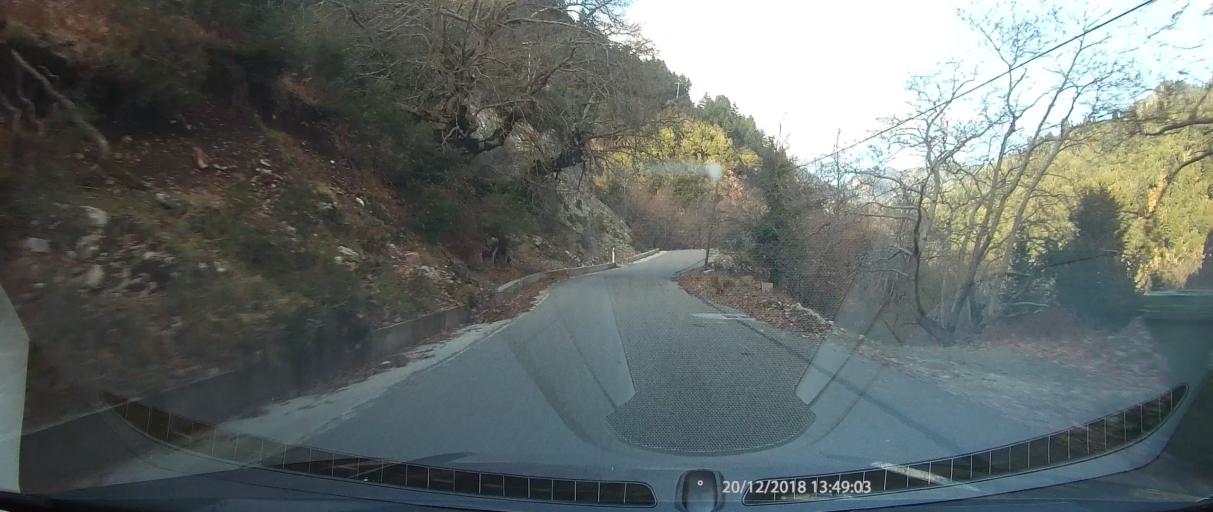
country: GR
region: West Greece
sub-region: Nomos Aitolias kai Akarnanias
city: Paravola
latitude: 38.6899
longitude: 21.6079
